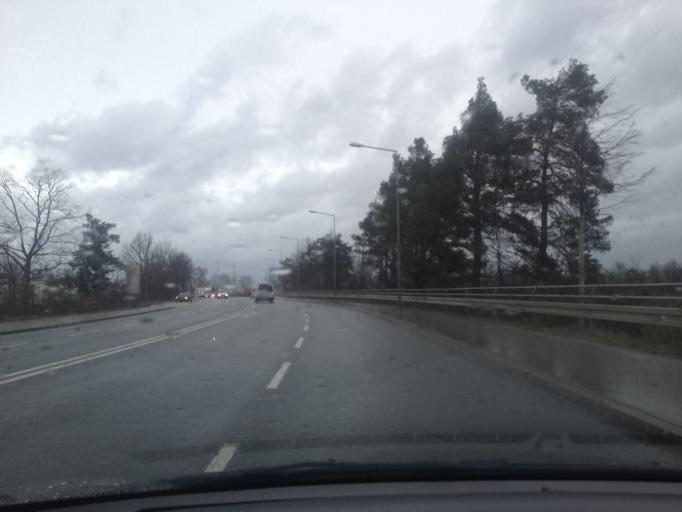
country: DE
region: Bavaria
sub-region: Regierungsbezirk Mittelfranken
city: Stein
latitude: 49.4044
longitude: 11.0538
